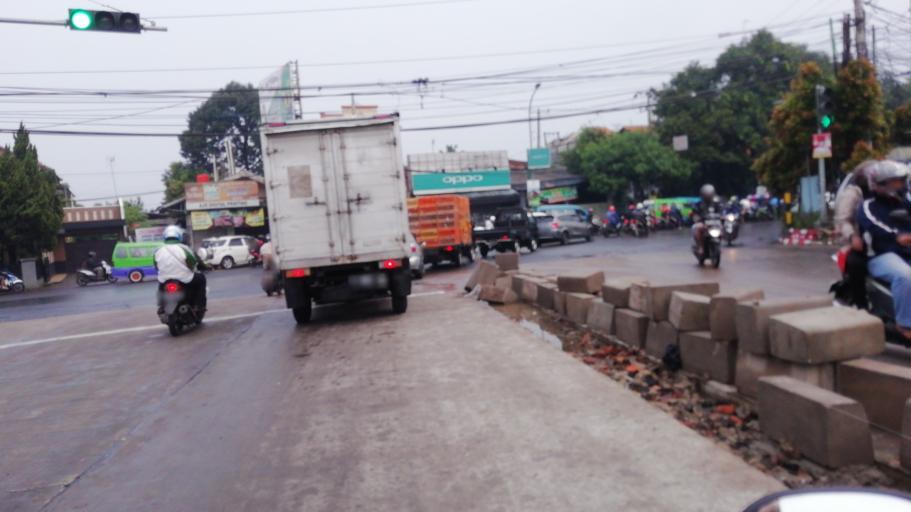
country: ID
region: West Java
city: Bogor
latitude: -6.5600
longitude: 106.8130
